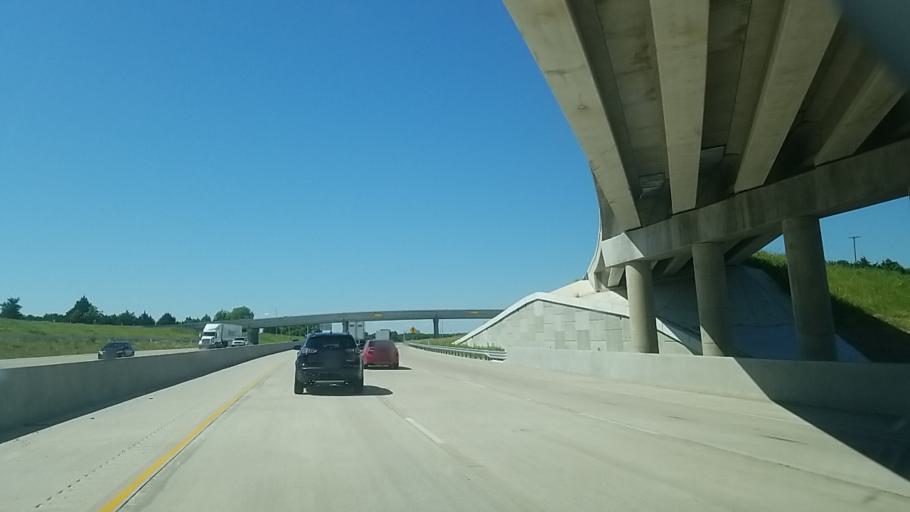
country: US
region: Texas
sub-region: Navarro County
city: Corsicana
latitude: 32.1515
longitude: -96.4672
